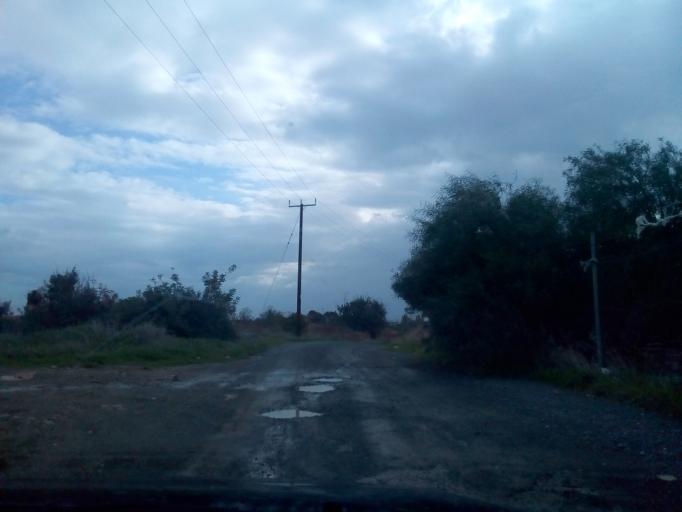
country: CY
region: Limassol
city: Ypsonas
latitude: 34.6777
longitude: 32.9725
